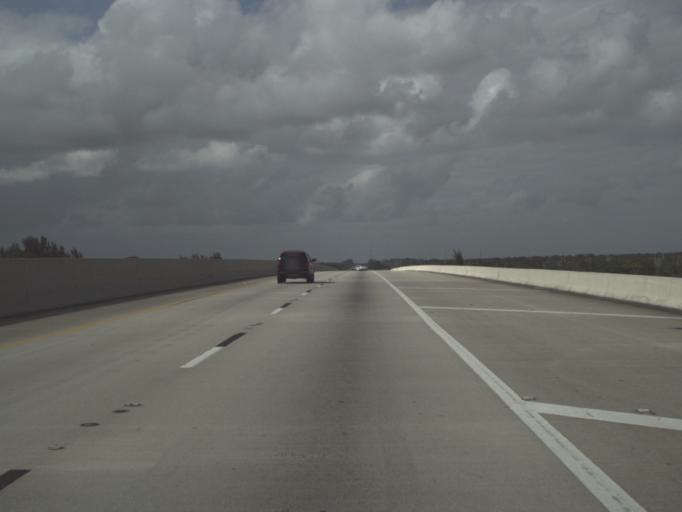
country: US
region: Florida
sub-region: Martin County
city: Palm City
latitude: 27.1171
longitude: -80.2743
